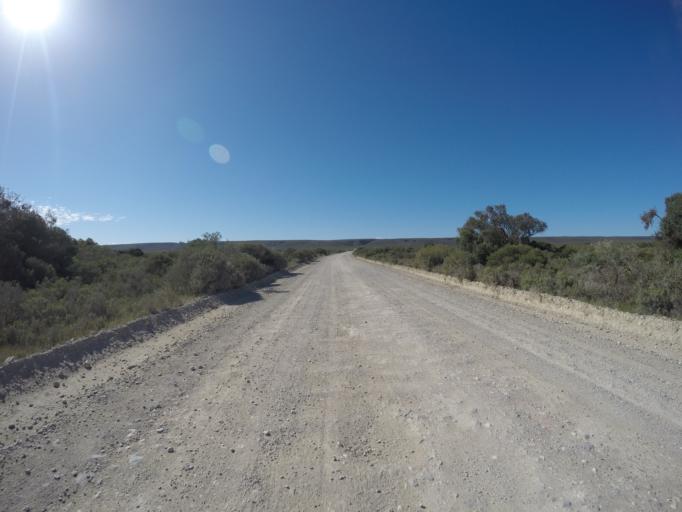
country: ZA
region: Western Cape
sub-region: Overberg District Municipality
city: Bredasdorp
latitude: -34.4477
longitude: 20.4225
